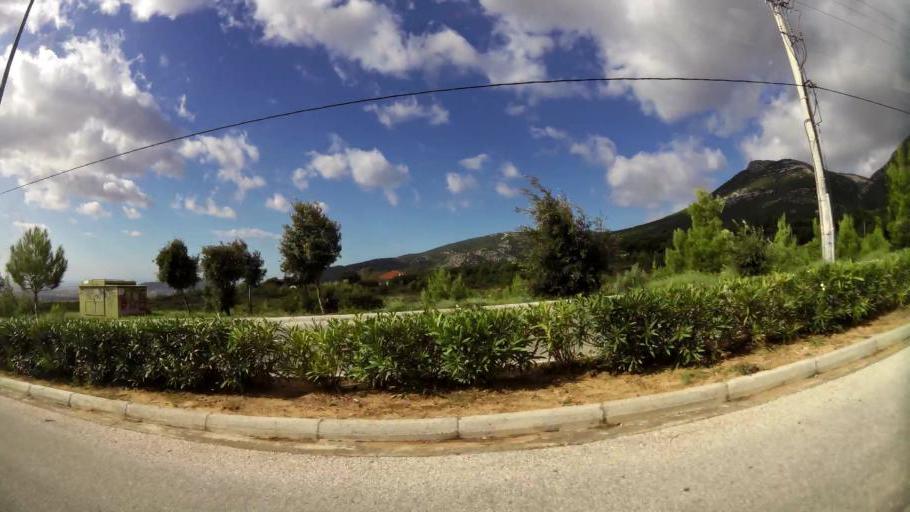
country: GR
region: Attica
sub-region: Nomarchia Anatolikis Attikis
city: Thrakomakedones
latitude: 38.1360
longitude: 23.7510
